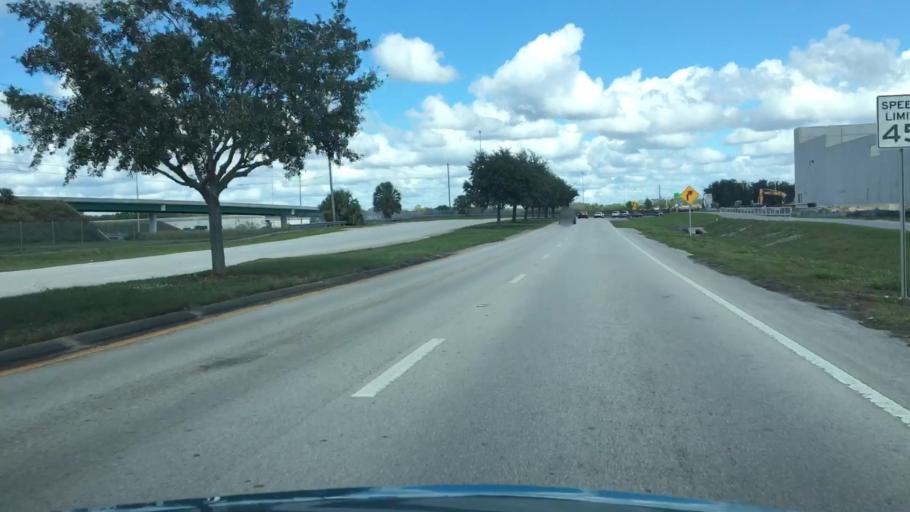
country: US
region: Florida
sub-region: Seminole County
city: Heathrow
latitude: 28.7875
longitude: -81.3472
